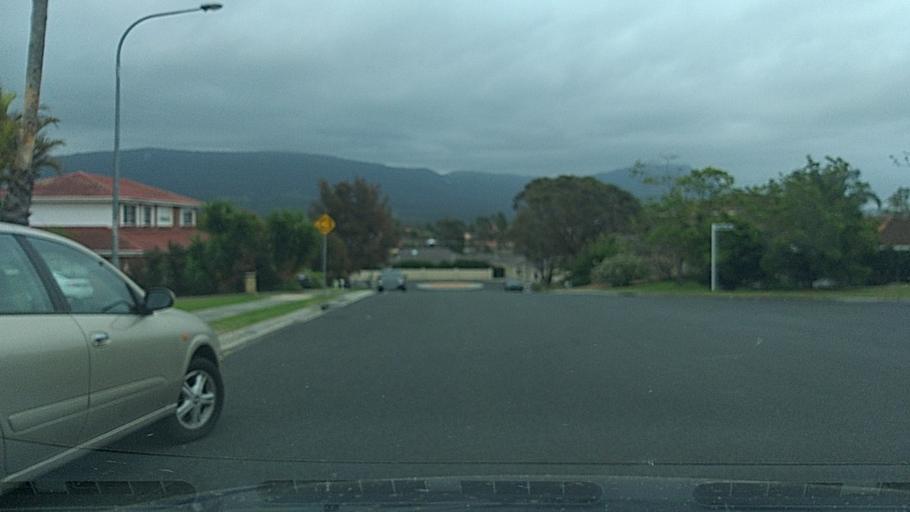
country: AU
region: New South Wales
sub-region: Wollongong
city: Dapto
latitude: -34.4914
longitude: 150.7743
